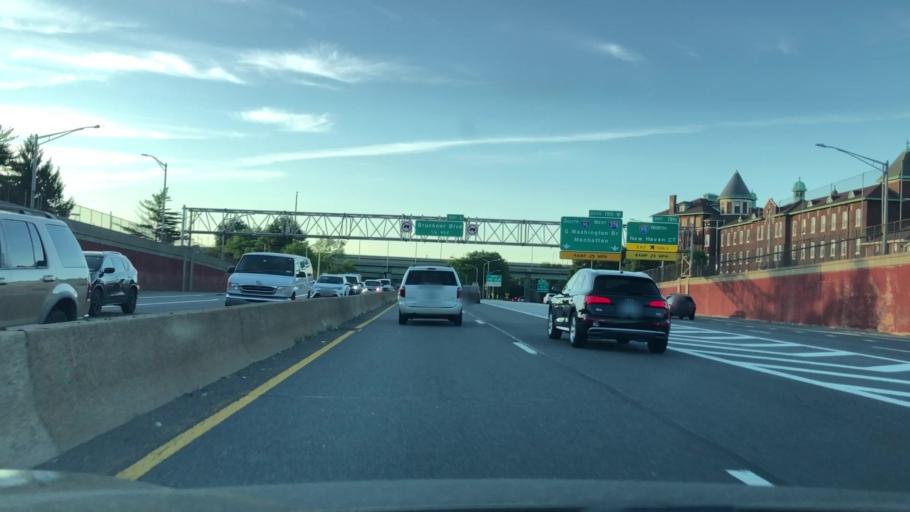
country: US
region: New York
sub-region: Bronx
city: The Bronx
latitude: 40.8251
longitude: -73.8350
